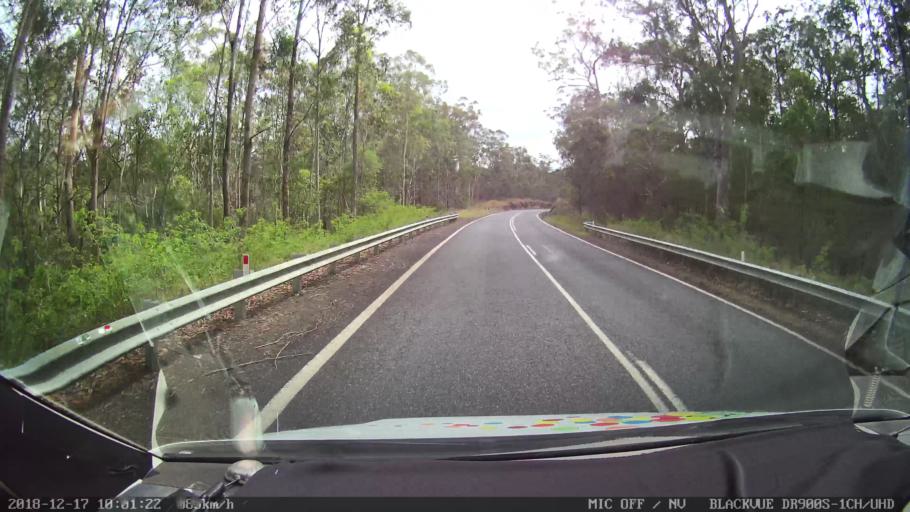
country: AU
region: New South Wales
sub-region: Tenterfield Municipality
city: Carrolls Creek
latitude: -28.9050
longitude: 152.4372
